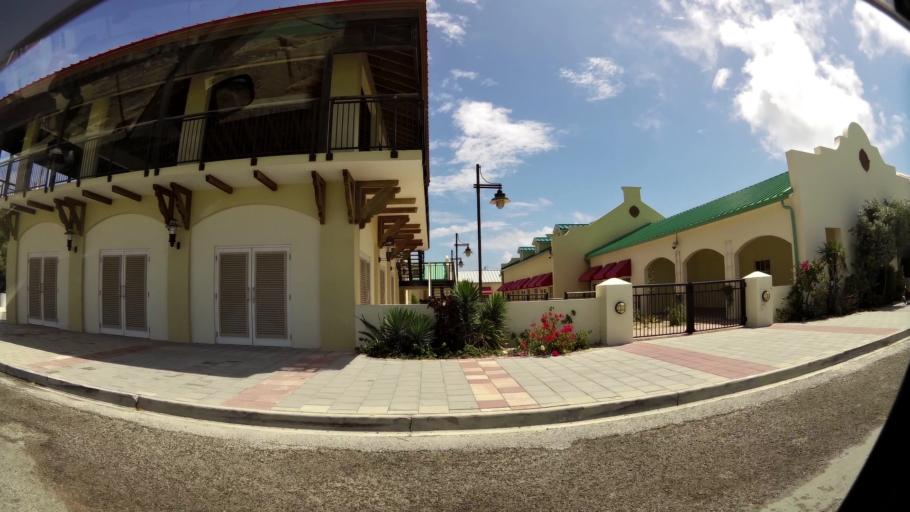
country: TC
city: Cockburn Town
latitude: 21.4696
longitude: -71.1469
